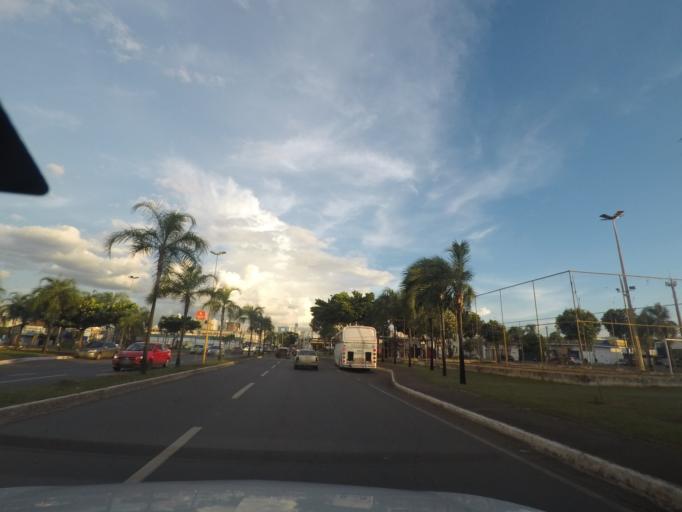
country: BR
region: Goias
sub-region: Goiania
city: Goiania
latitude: -16.6783
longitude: -49.2860
